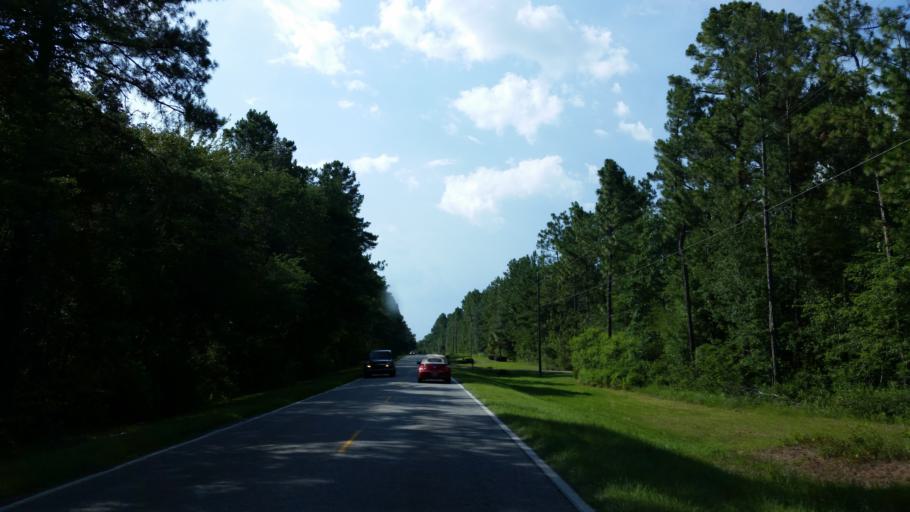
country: US
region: Georgia
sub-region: Lowndes County
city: Hahira
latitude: 30.9097
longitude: -83.3831
